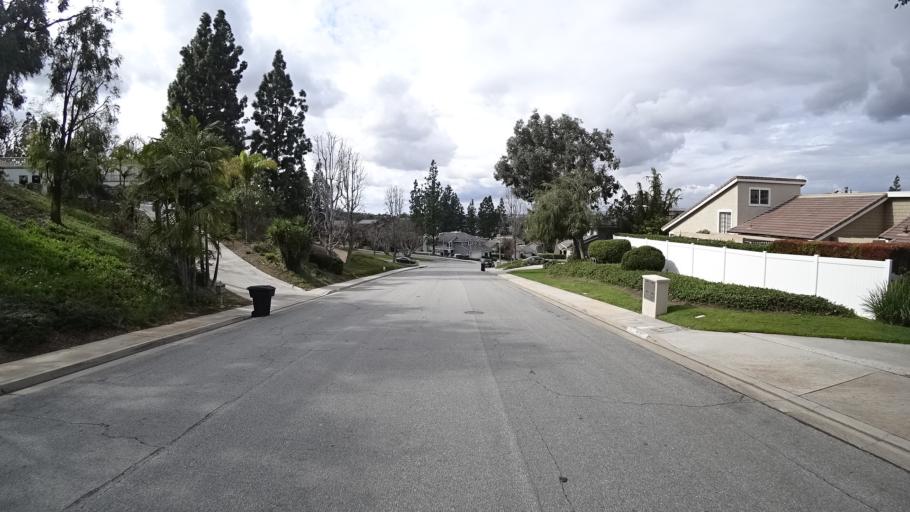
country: US
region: California
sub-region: Orange County
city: Villa Park
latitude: 33.8418
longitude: -117.7883
